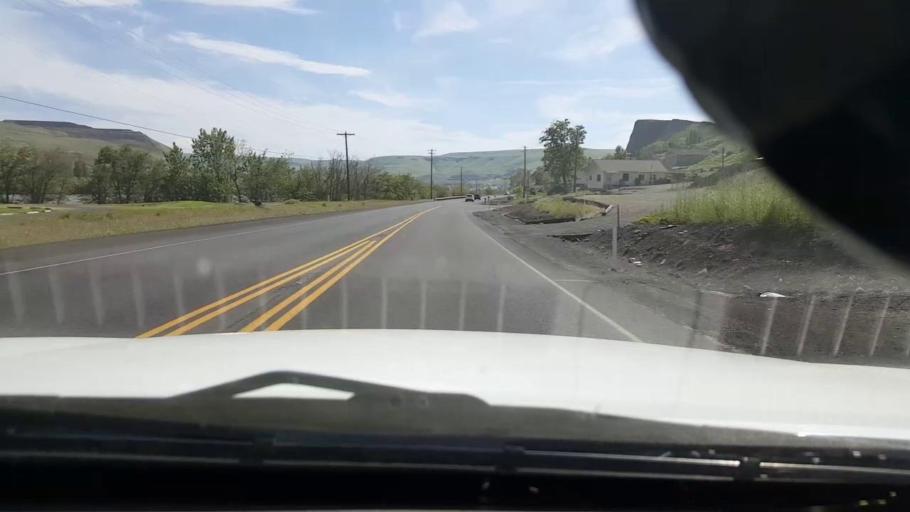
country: US
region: Washington
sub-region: Asotin County
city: West Clarkston-Highland
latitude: 46.3809
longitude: -117.0511
